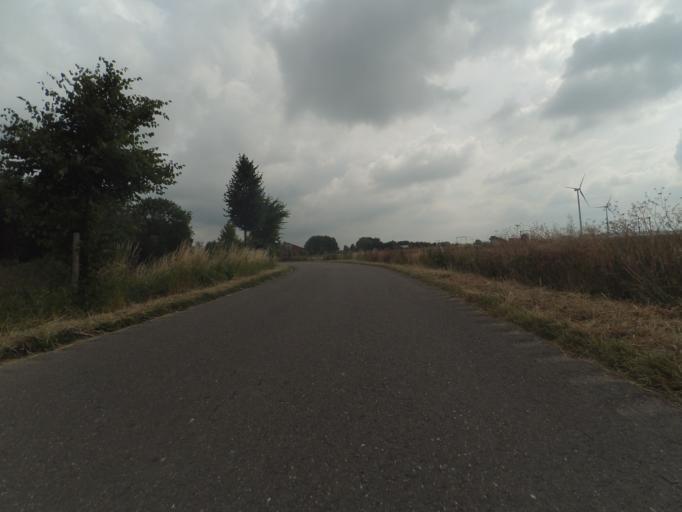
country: NL
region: North Brabant
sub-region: Gemeente Moerdijk
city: Klundert
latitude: 51.6222
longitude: 4.5880
